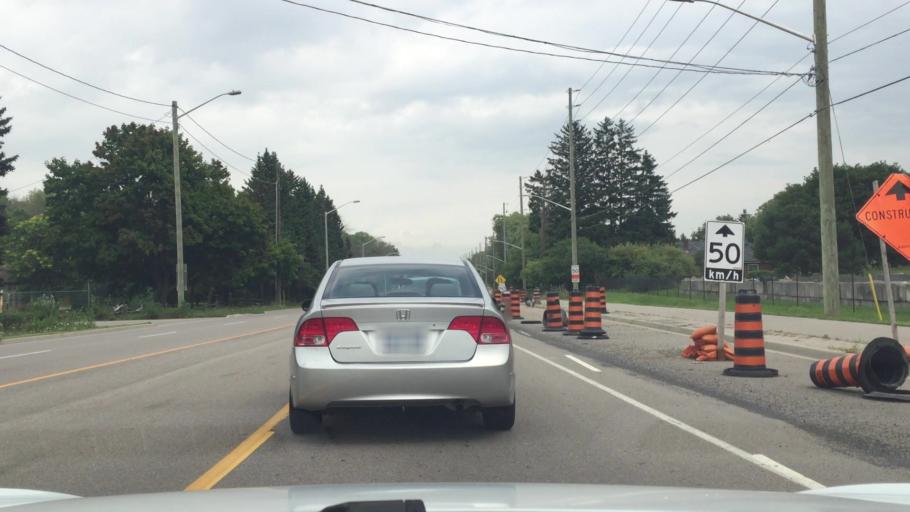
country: CA
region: Ontario
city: Ajax
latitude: 43.8533
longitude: -78.9758
